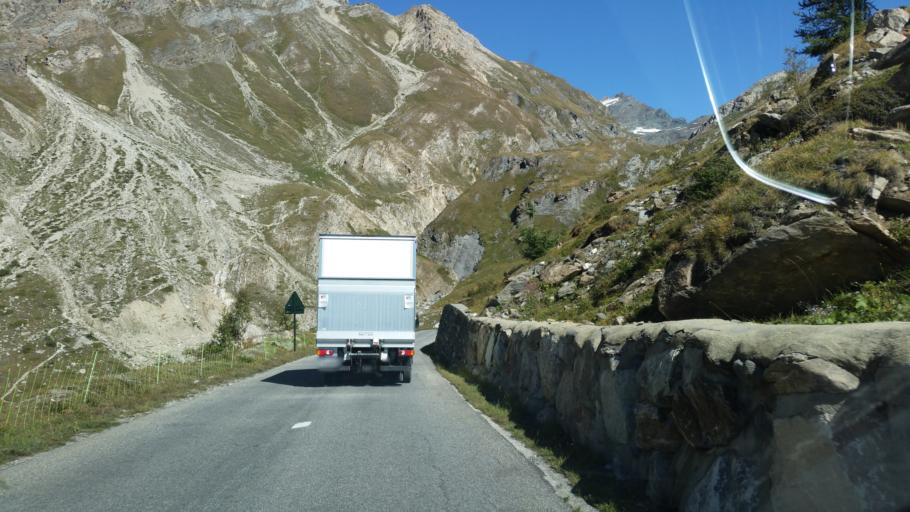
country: FR
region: Rhone-Alpes
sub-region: Departement de la Savoie
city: Val-d'Isere
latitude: 45.4528
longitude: 7.0368
